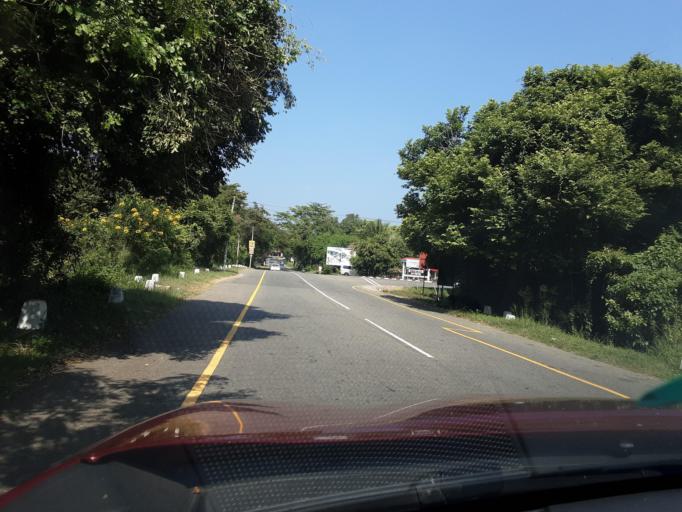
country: LK
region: Uva
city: Badulla
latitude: 7.2828
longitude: 81.0436
